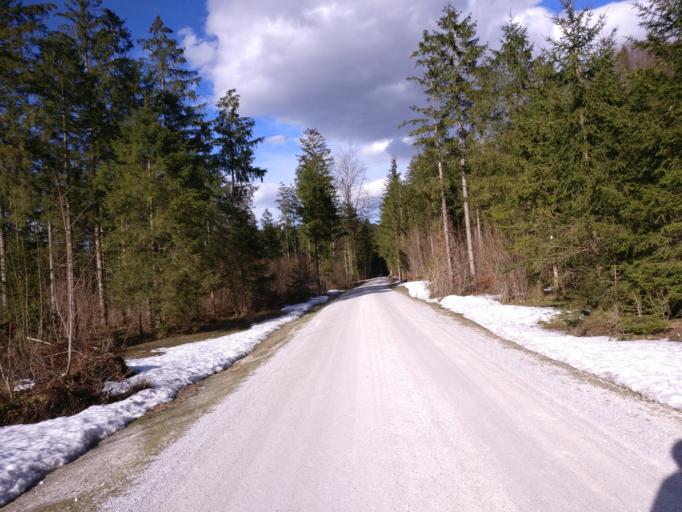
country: AT
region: Salzburg
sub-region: Politischer Bezirk Hallein
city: Golling an der Salzach
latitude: 47.5800
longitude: 13.1465
